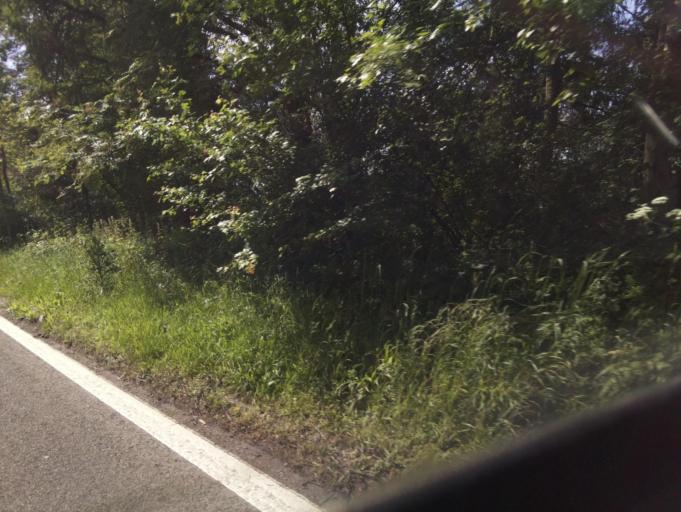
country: GB
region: England
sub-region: North Lincolnshire
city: Broughton
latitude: 53.5482
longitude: -0.5788
